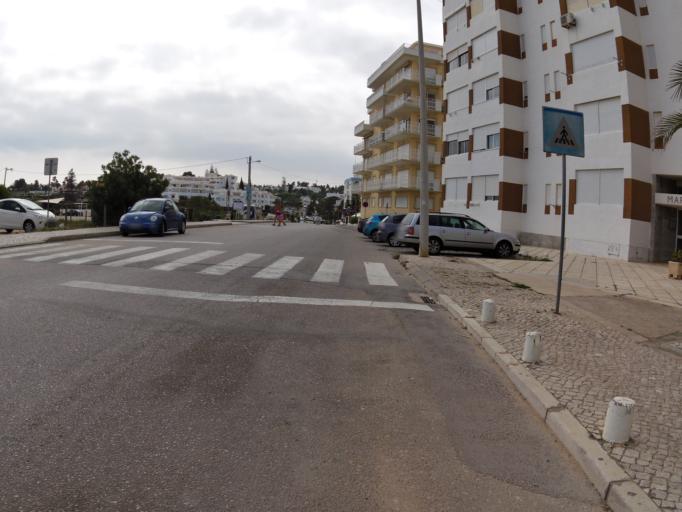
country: PT
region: Faro
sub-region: Silves
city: Armacao de Pera
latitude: 37.1031
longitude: -8.3681
